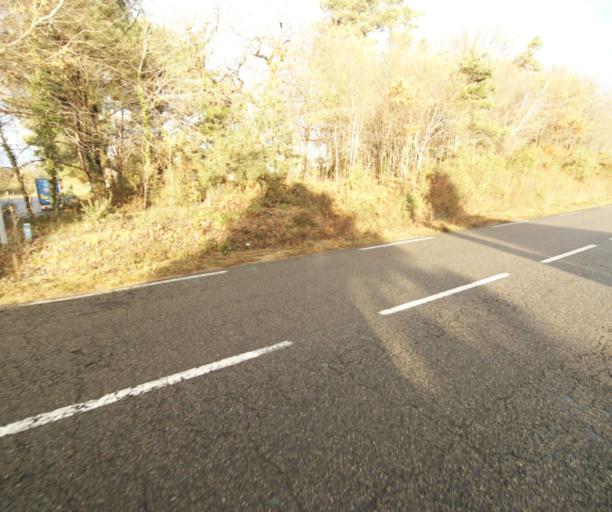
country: FR
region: Limousin
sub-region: Departement de la Correze
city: Saint-Mexant
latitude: 45.2564
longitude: 1.6345
